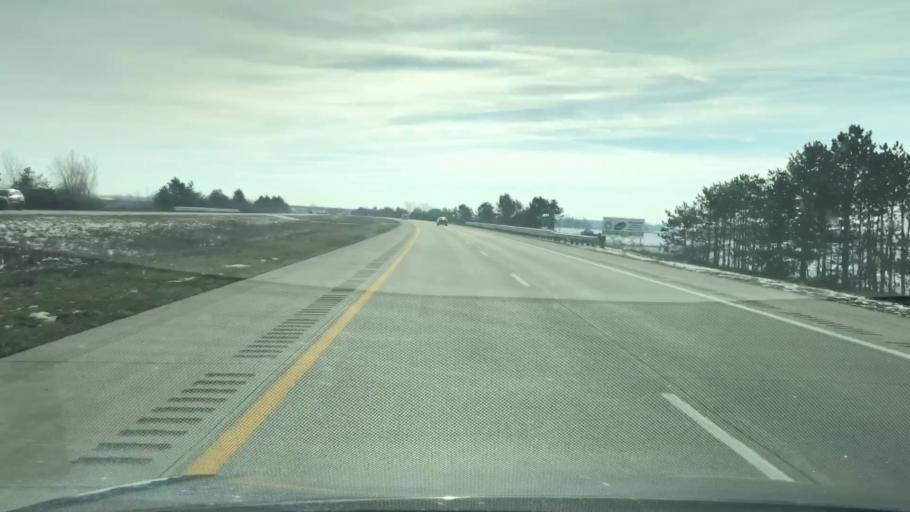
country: US
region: Michigan
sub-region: Bay County
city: Pinconning
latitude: 43.8768
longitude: -84.0222
